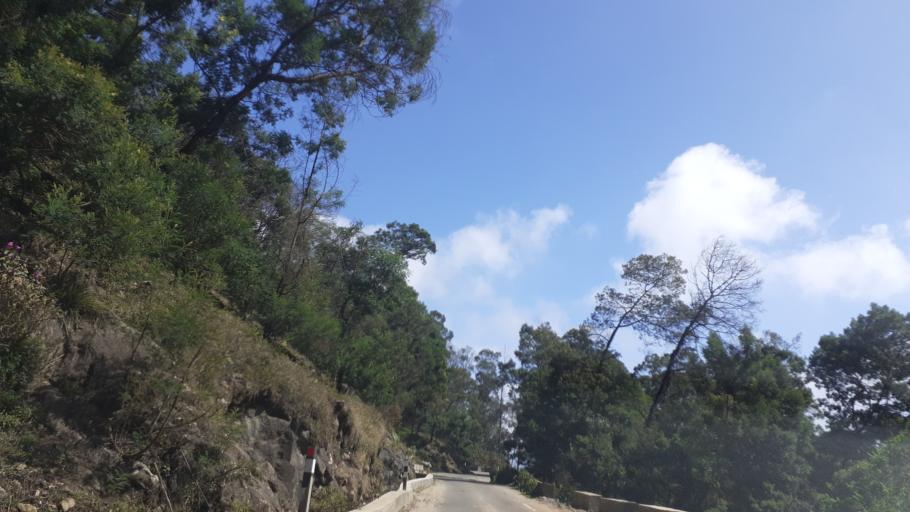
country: IN
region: Tamil Nadu
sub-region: Dindigul
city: Kodaikanal
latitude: 10.2258
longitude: 77.4224
